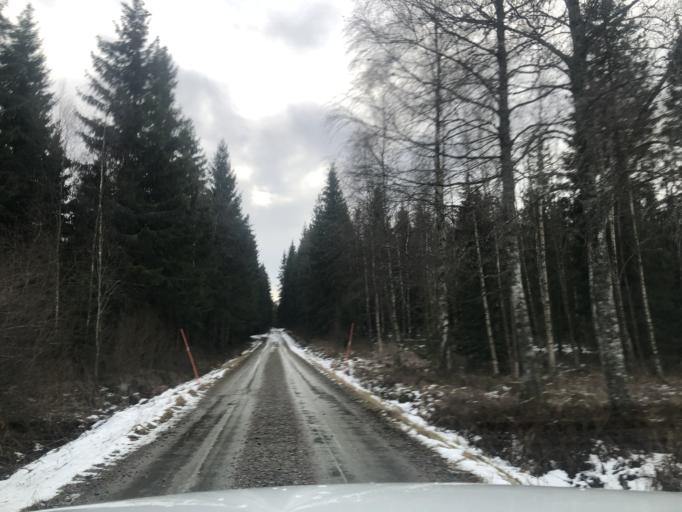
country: SE
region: Vaestra Goetaland
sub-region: Ulricehamns Kommun
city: Ulricehamn
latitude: 57.7874
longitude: 13.4830
